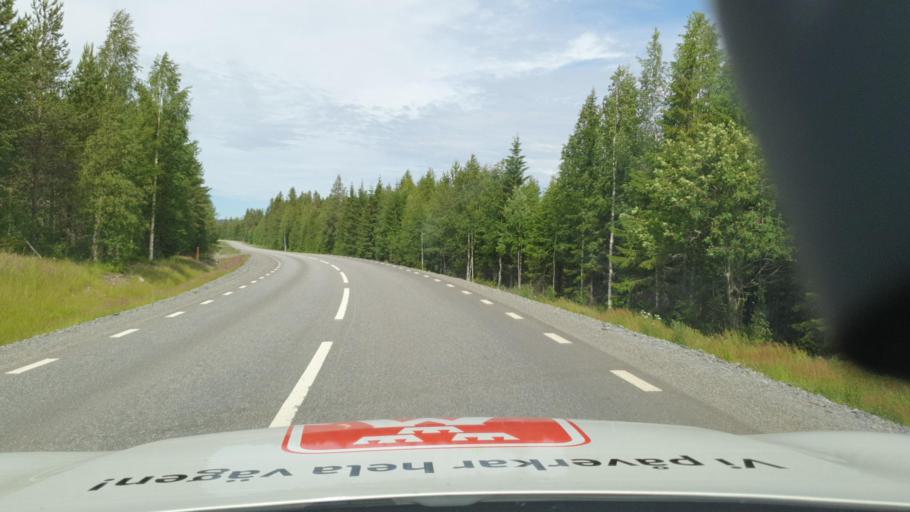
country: SE
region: Vaesterbotten
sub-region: Skelleftea Kommun
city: Burtraesk
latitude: 64.3959
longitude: 20.5486
